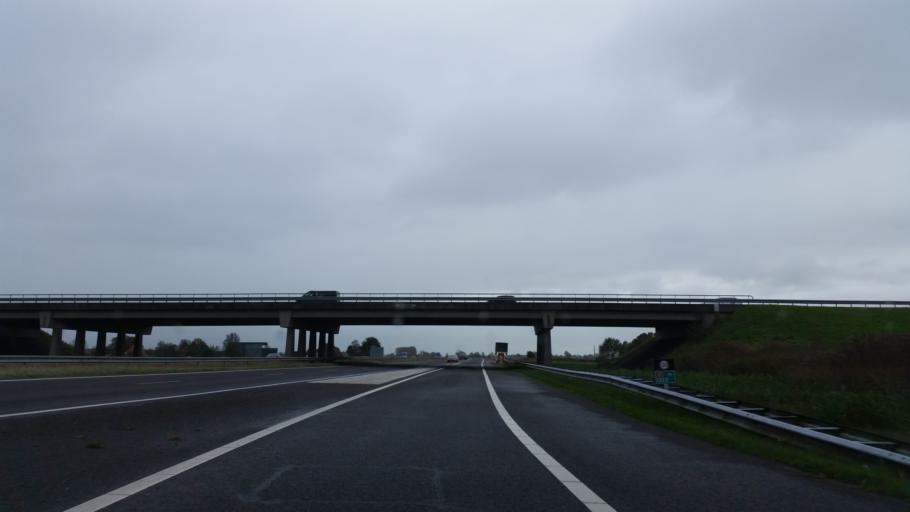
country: NL
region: Friesland
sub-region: Gemeente Skarsterlan
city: Joure
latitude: 52.9632
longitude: 5.7687
